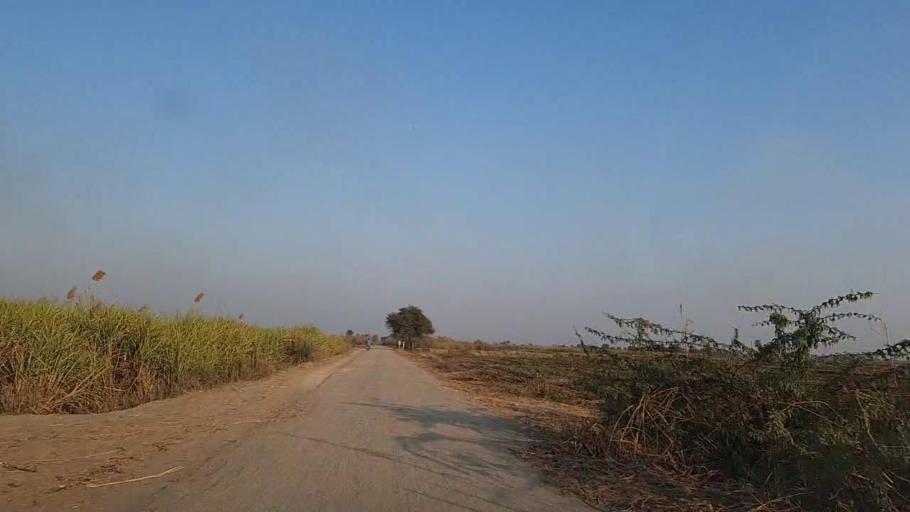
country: PK
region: Sindh
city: Daur
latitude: 26.5106
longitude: 68.2989
